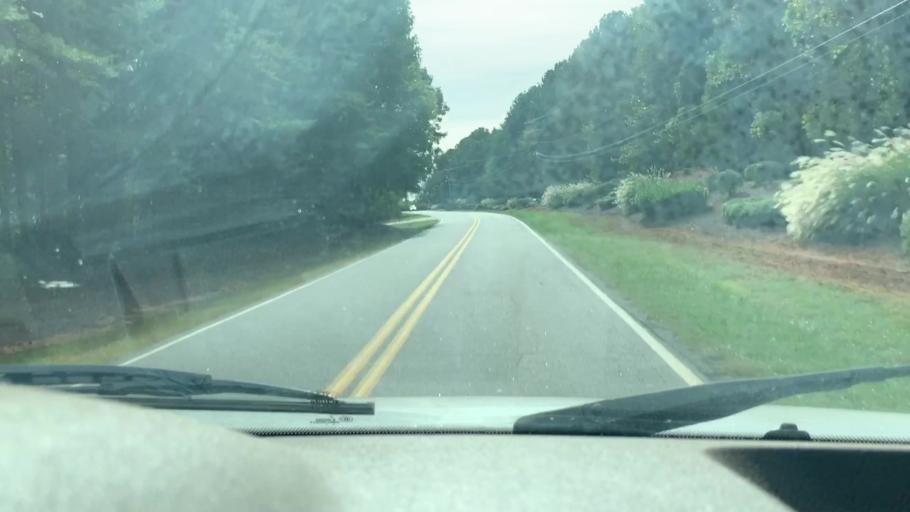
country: US
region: North Carolina
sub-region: Catawba County
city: Lake Norman of Catawba
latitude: 35.5700
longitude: -80.9350
